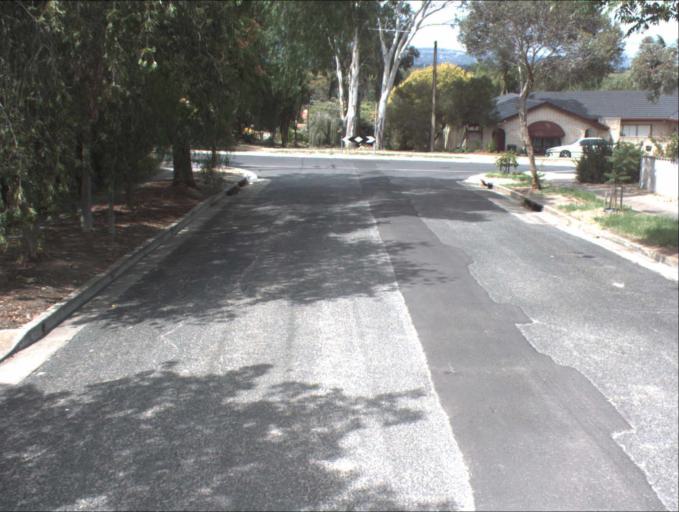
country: AU
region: South Australia
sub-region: Campbelltown
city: Paradise
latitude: -34.8611
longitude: 138.6651
